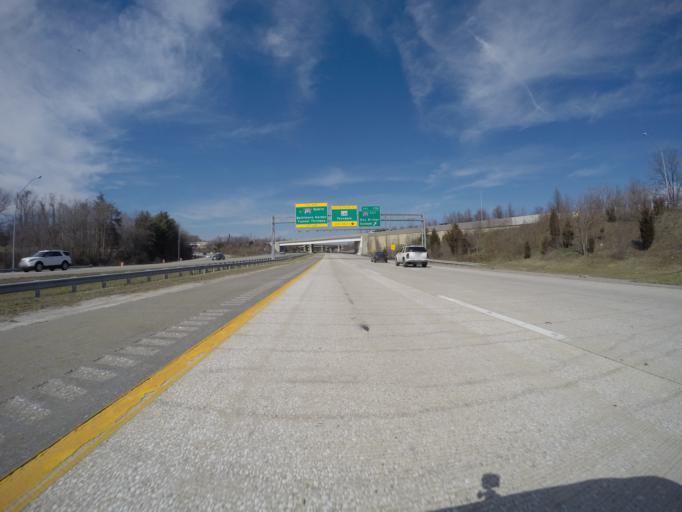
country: US
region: Maryland
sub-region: Anne Arundel County
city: Ferndale
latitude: 39.1968
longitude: -76.6321
